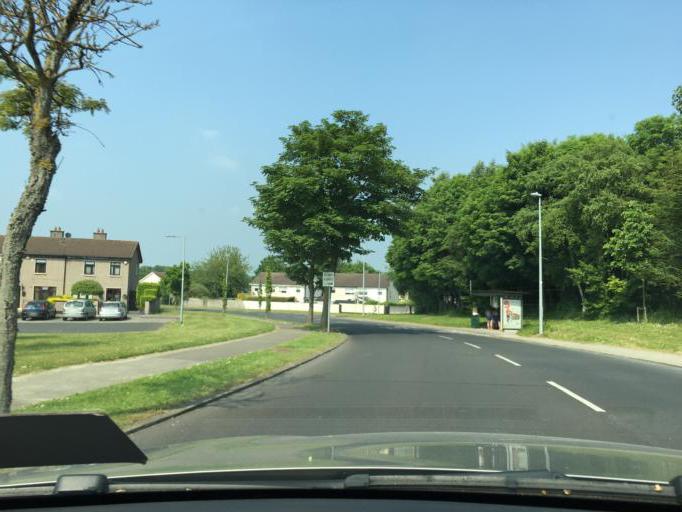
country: IE
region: Leinster
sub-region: Fingal County
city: Blanchardstown
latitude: 53.3977
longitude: -6.3720
